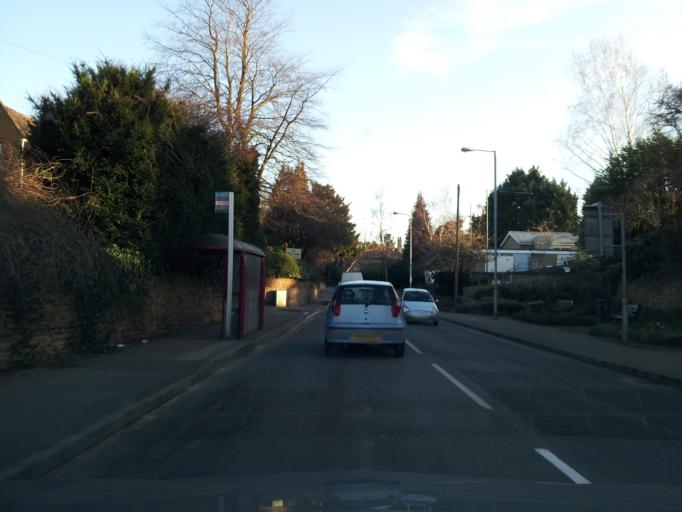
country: GB
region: England
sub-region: Northamptonshire
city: Northampton
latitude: 52.2453
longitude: -0.9479
